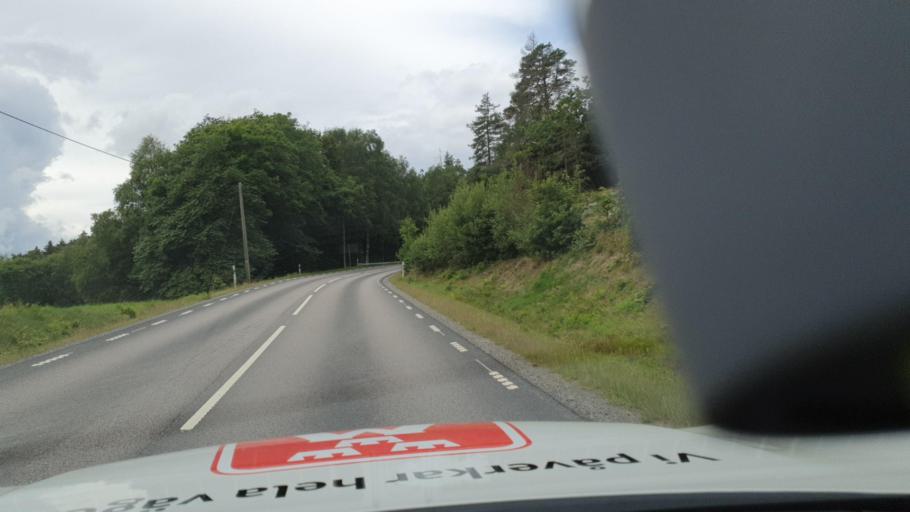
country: SE
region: Vaestra Goetaland
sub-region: Harryda Kommun
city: Landvetter
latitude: 57.6818
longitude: 12.1802
